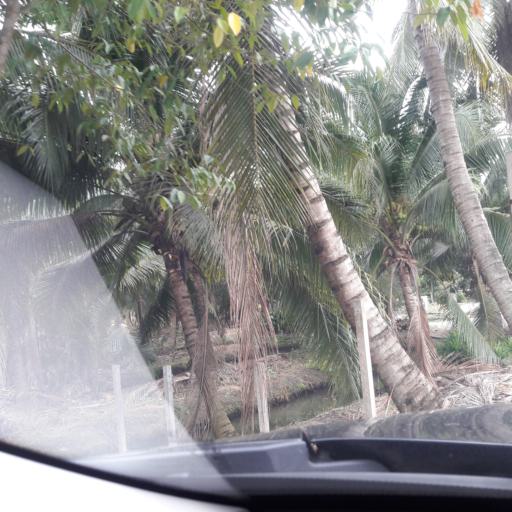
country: TH
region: Ratchaburi
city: Damnoen Saduak
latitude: 13.5851
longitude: 99.9416
